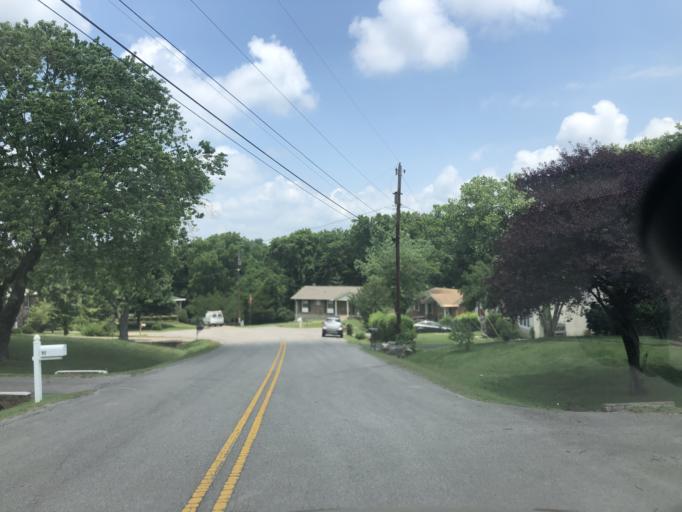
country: US
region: Tennessee
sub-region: Davidson County
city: Lakewood
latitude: 36.2098
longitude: -86.6356
